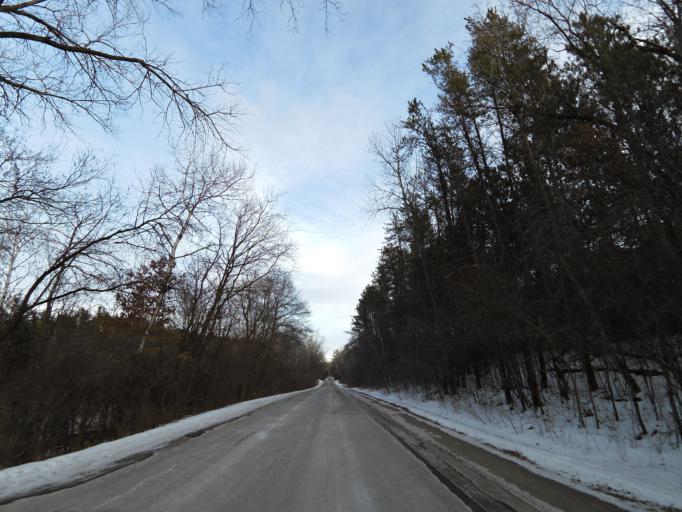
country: US
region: Minnesota
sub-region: Washington County
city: Afton
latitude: 44.9126
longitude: -92.8352
